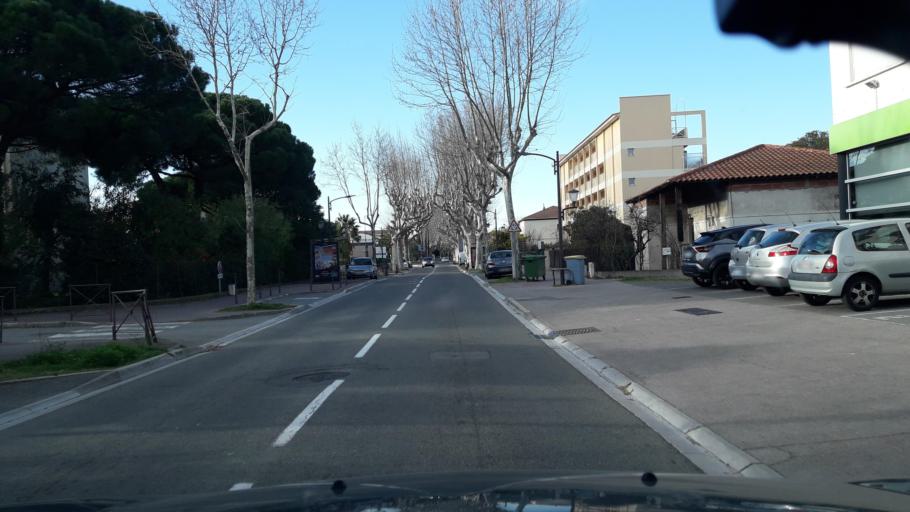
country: FR
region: Provence-Alpes-Cote d'Azur
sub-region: Departement du Var
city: Frejus
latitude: 43.4245
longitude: 6.7400
